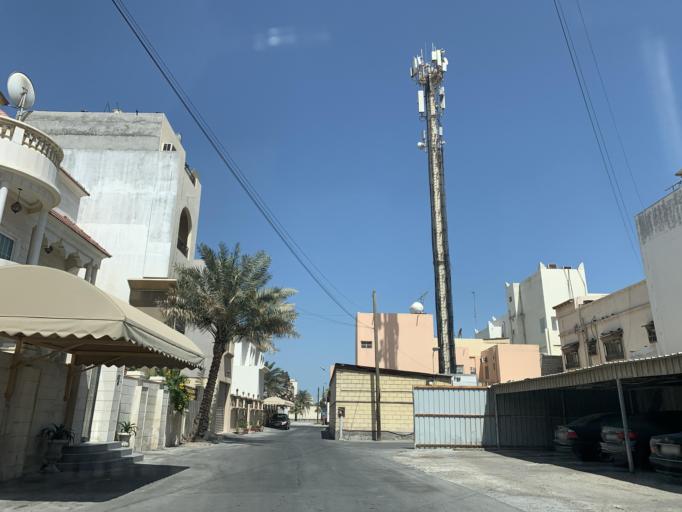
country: BH
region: Muharraq
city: Al Muharraq
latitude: 26.2659
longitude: 50.6187
